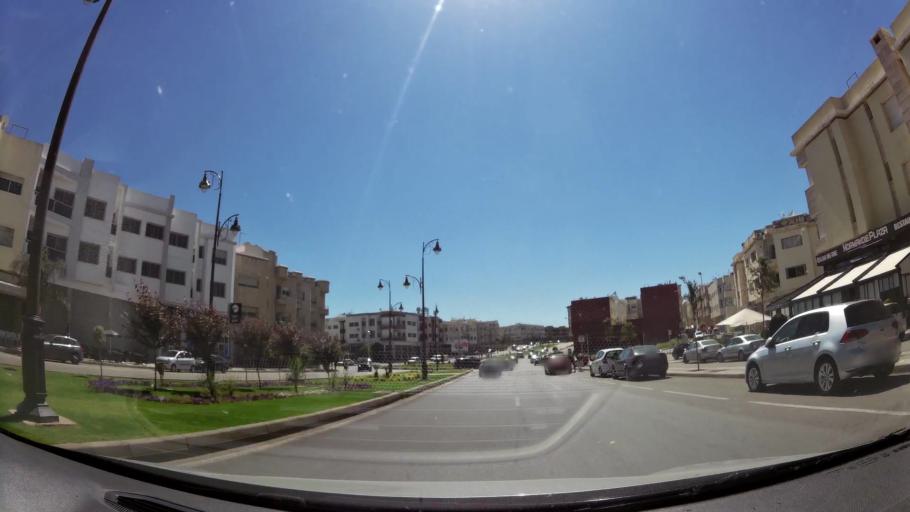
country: MA
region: Fes-Boulemane
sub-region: Fes
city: Fes
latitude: 34.0141
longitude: -5.0023
